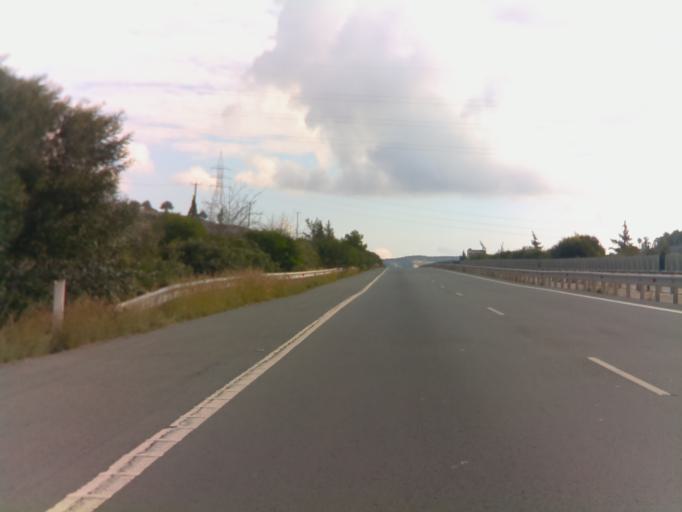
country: CY
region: Limassol
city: Pyrgos
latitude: 34.7189
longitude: 33.1812
